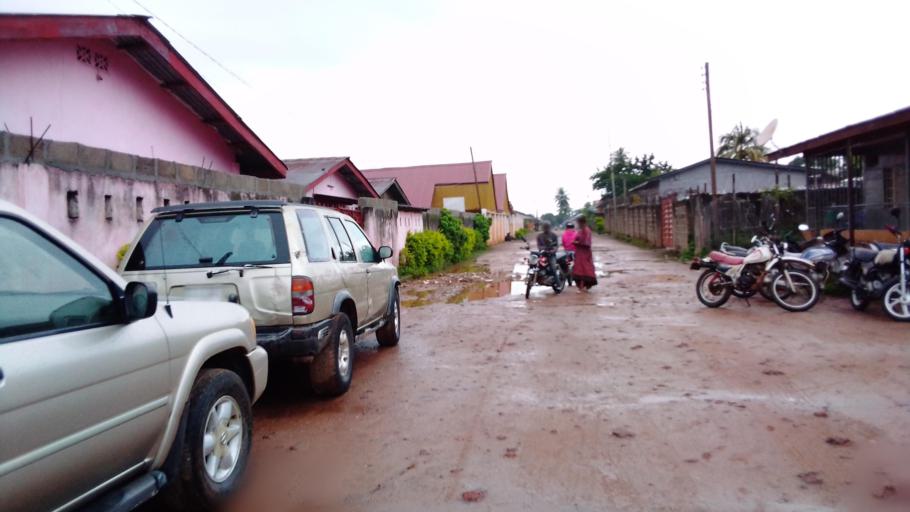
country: SL
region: Eastern Province
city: Kenema
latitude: 7.8907
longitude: -11.1883
